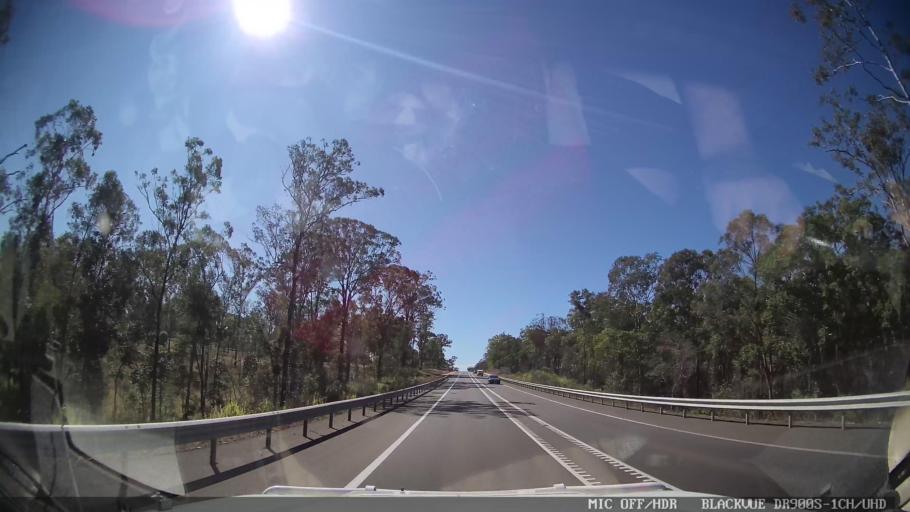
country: AU
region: Queensland
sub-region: Fraser Coast
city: Maryborough
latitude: -25.6538
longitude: 152.6300
